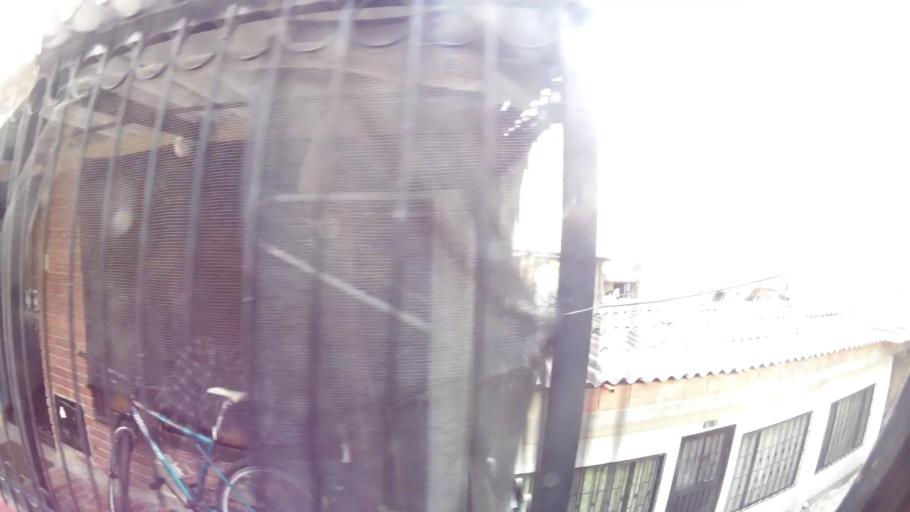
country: CO
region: Cundinamarca
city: Cota
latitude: 4.7272
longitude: -74.0861
